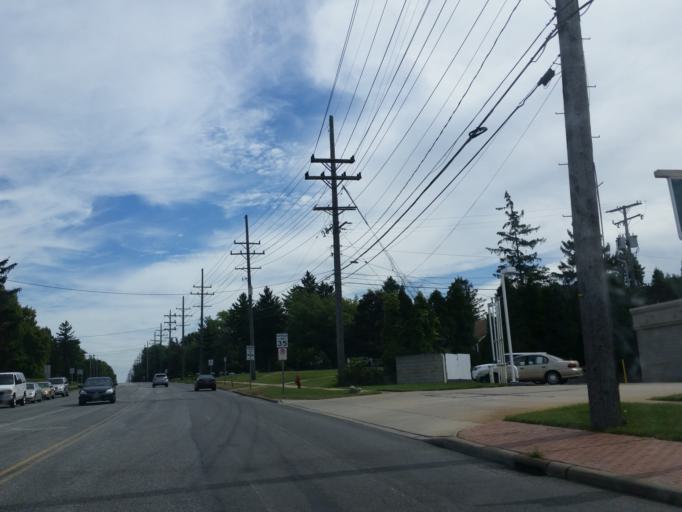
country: US
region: Ohio
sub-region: Cuyahoga County
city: Seven Hills
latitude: 41.3615
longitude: -81.6842
